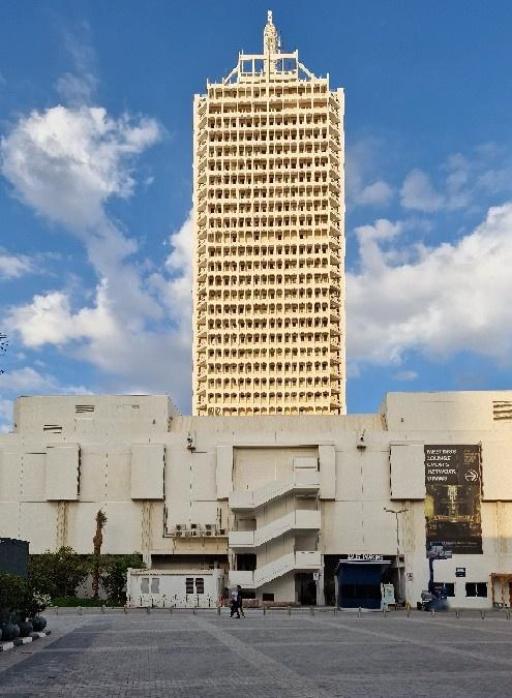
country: AE
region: Ash Shariqah
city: Sharjah
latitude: 25.2269
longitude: 55.2879
